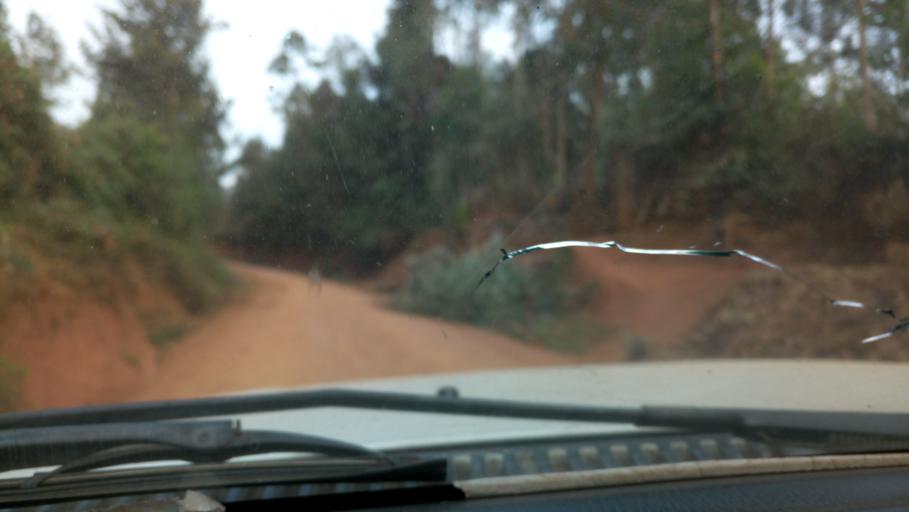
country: KE
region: Murang'a District
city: Maragua
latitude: -0.8409
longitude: 37.0019
